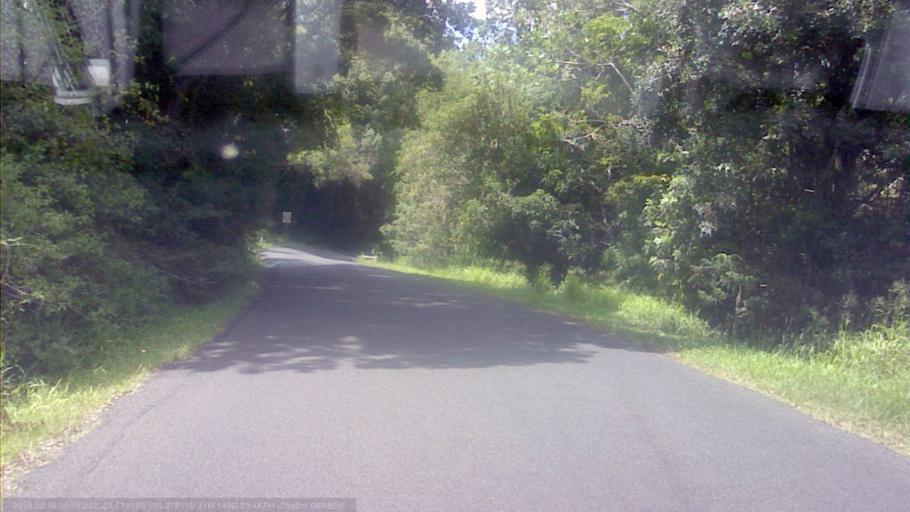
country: AU
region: New South Wales
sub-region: Lismore Municipality
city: Nimbin
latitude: -28.6741
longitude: 153.2781
